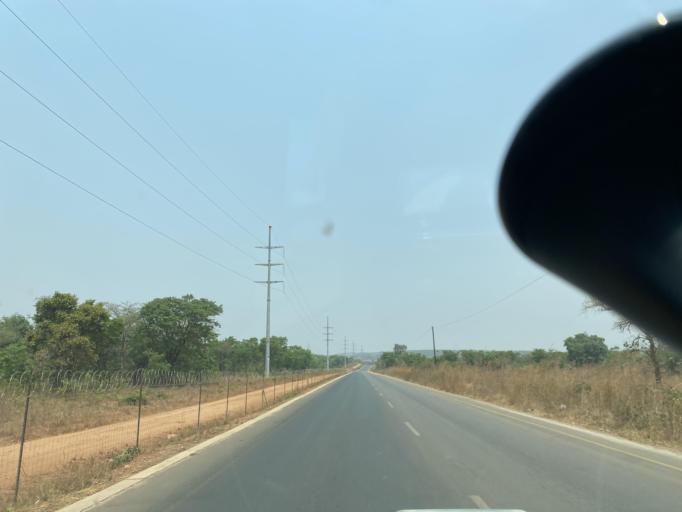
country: ZM
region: Lusaka
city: Lusaka
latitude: -15.5350
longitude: 28.4698
